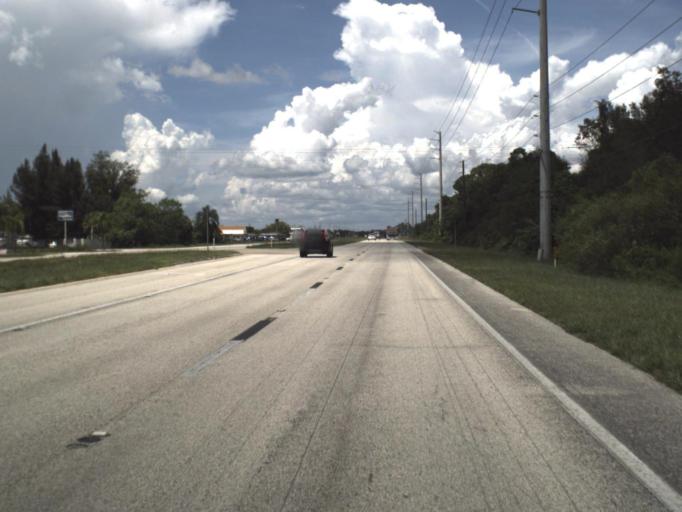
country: US
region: Florida
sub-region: Charlotte County
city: Charlotte Park
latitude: 26.8697
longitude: -82.0009
